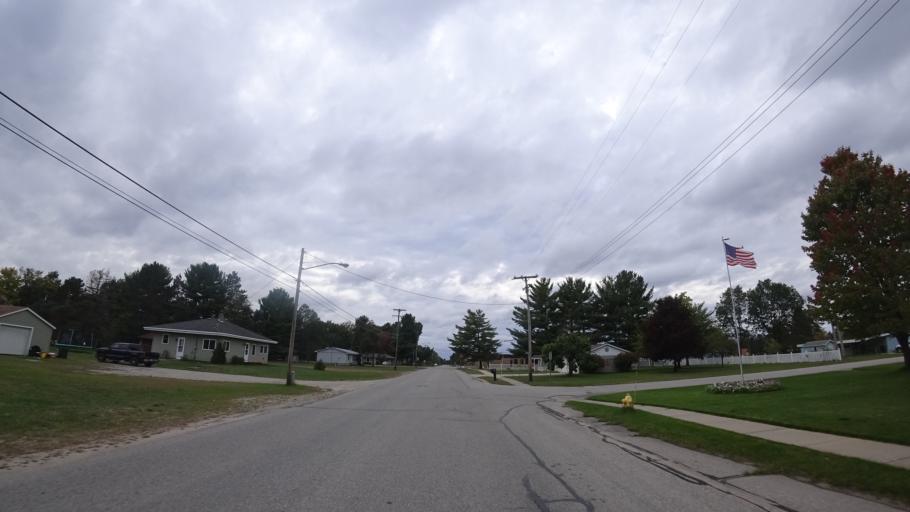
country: US
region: Michigan
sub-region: Kalkaska County
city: Kalkaska
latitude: 44.7355
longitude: -85.1829
